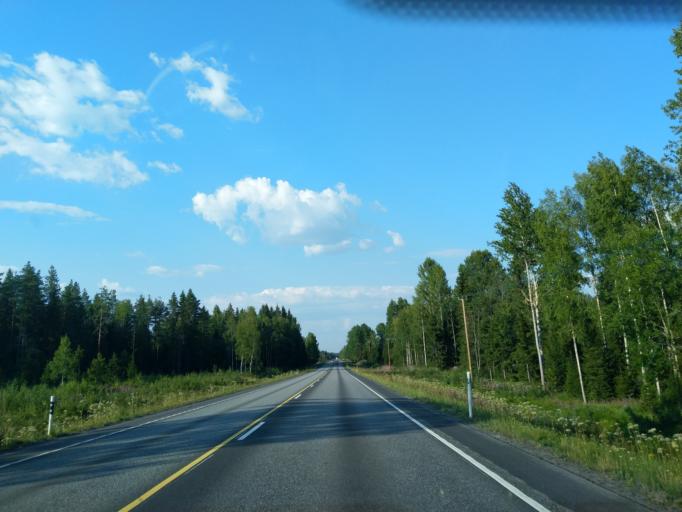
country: FI
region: Satakunta
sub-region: Pori
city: Pomarkku
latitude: 61.7295
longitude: 22.0697
